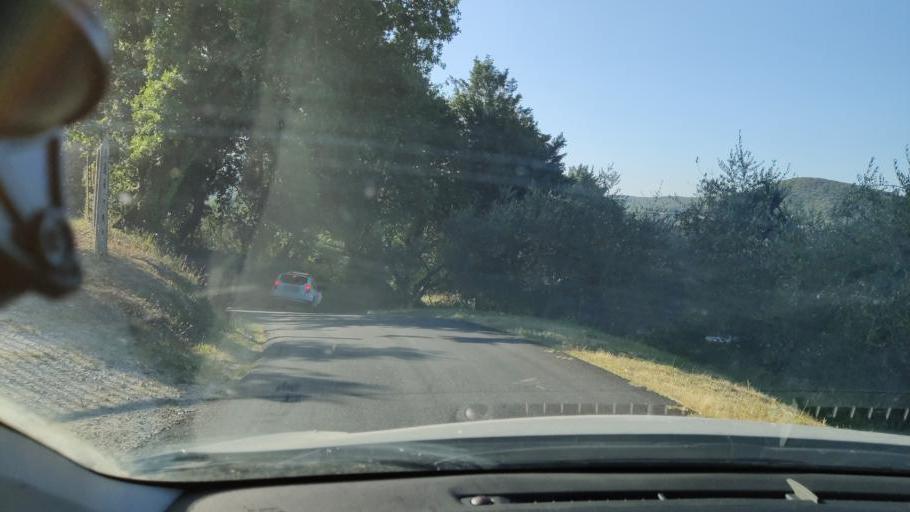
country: IT
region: Umbria
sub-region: Provincia di Terni
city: Amelia
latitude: 42.5431
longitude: 12.3999
